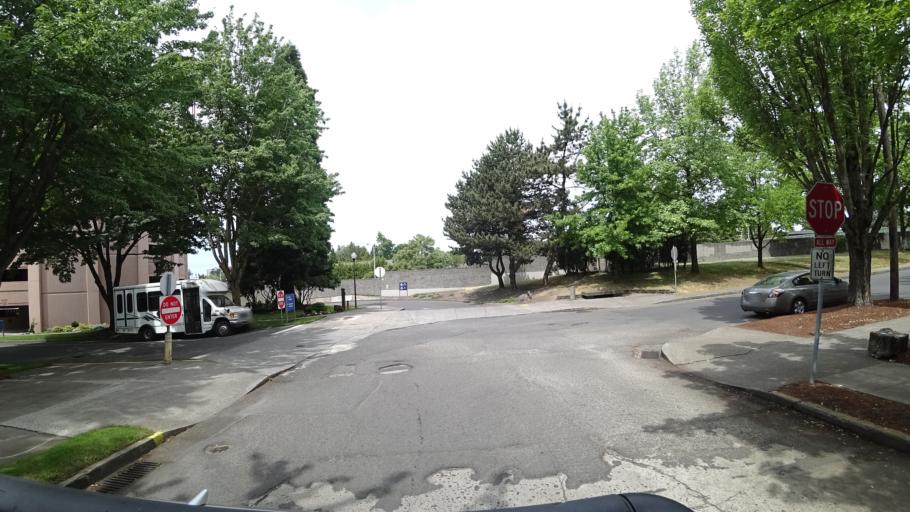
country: US
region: Oregon
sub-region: Multnomah County
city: Lents
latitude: 45.5272
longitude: -122.6101
